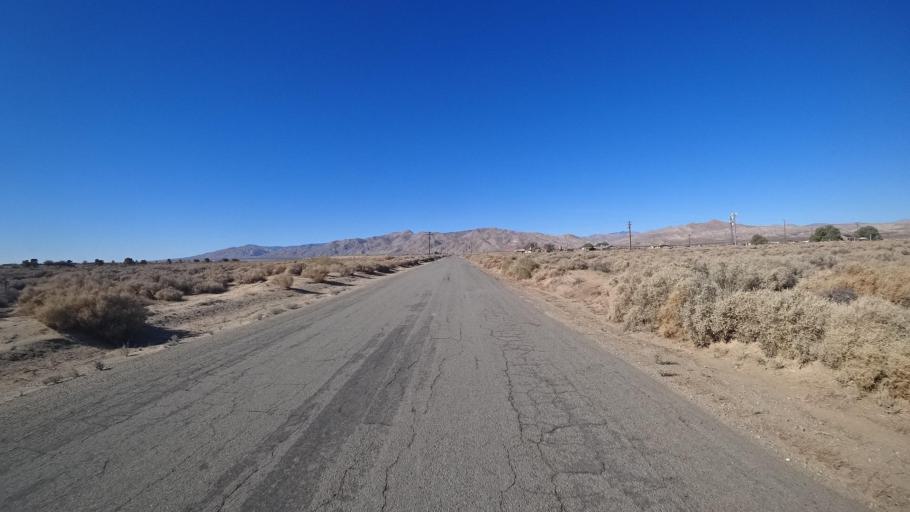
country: US
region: California
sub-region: Kern County
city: California City
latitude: 35.2869
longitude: -117.9665
